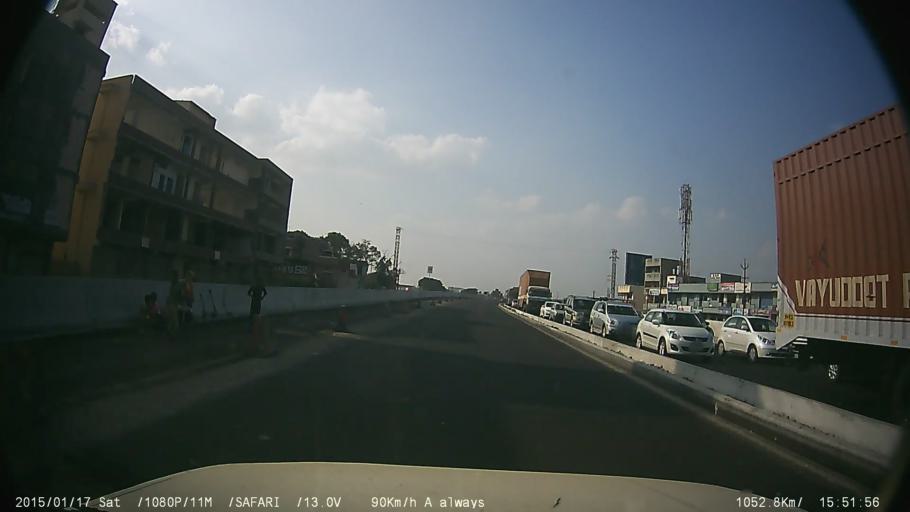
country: IN
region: Tamil Nadu
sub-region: Krishnagiri
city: Hosur
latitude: 12.7377
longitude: 77.8229
